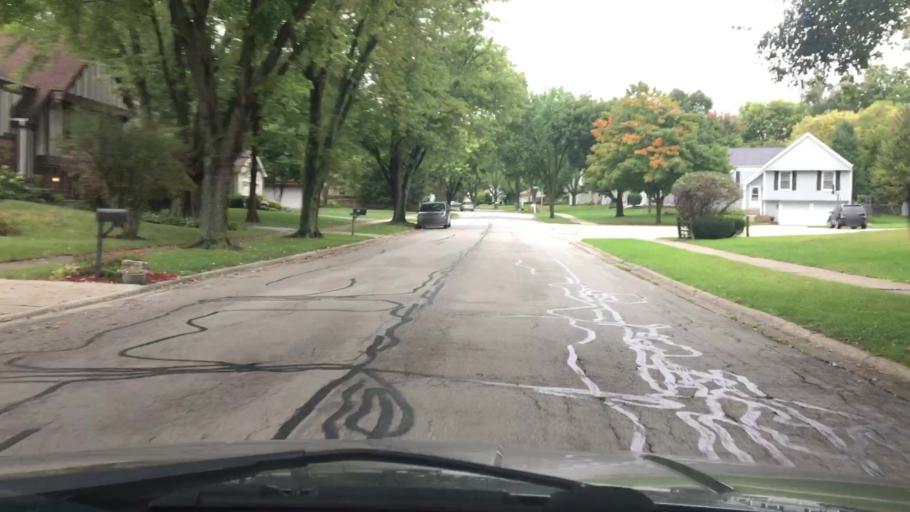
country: US
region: Illinois
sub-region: DuPage County
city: Naperville
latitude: 41.7331
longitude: -88.1328
